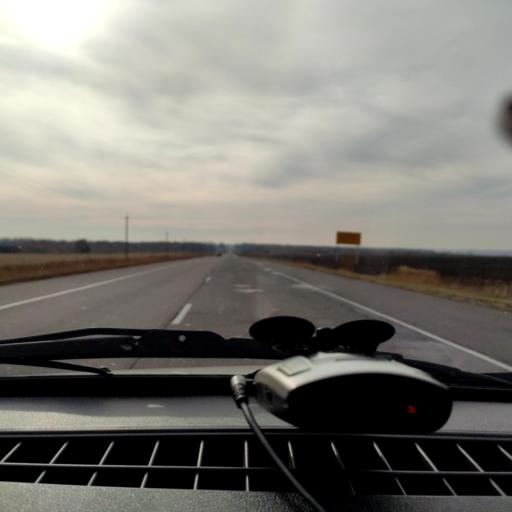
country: RU
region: Voronezj
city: Strelitsa
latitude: 51.5279
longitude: 38.9692
